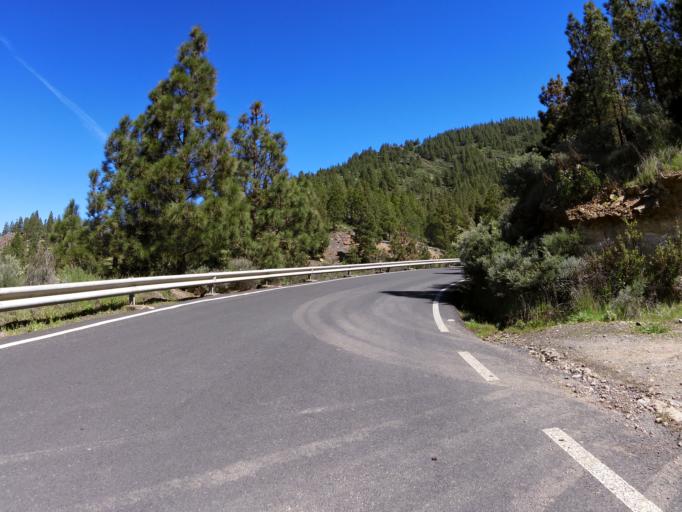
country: ES
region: Canary Islands
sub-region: Provincia de Las Palmas
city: Artenara
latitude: 28.0208
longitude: -15.6699
